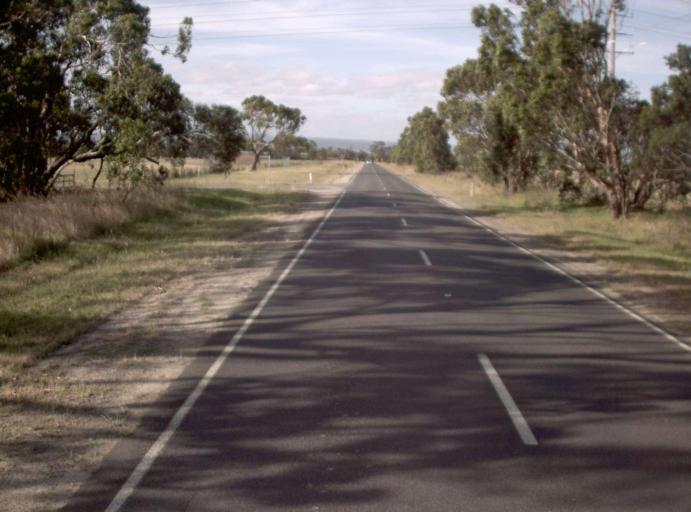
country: AU
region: Victoria
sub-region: Latrobe
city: Traralgon
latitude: -38.2225
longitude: 146.5210
